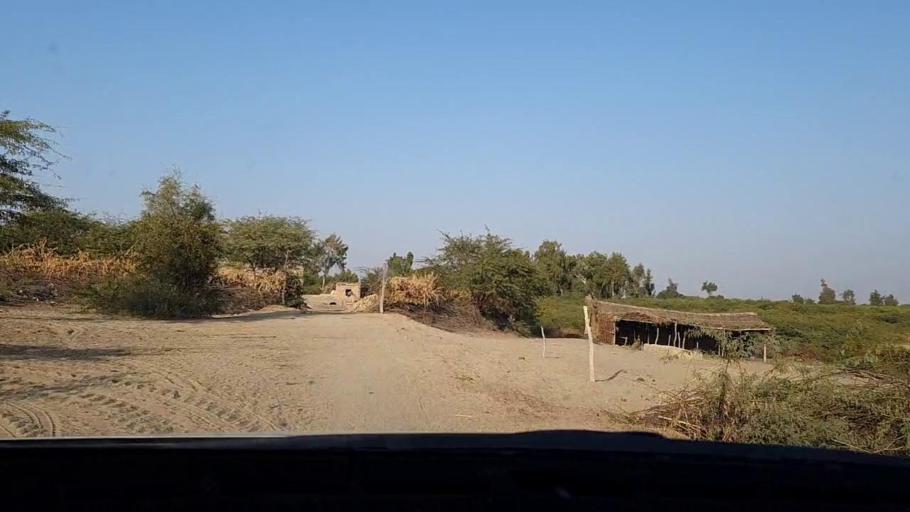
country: PK
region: Sindh
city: Tando Mittha Khan
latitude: 25.8602
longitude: 69.3168
